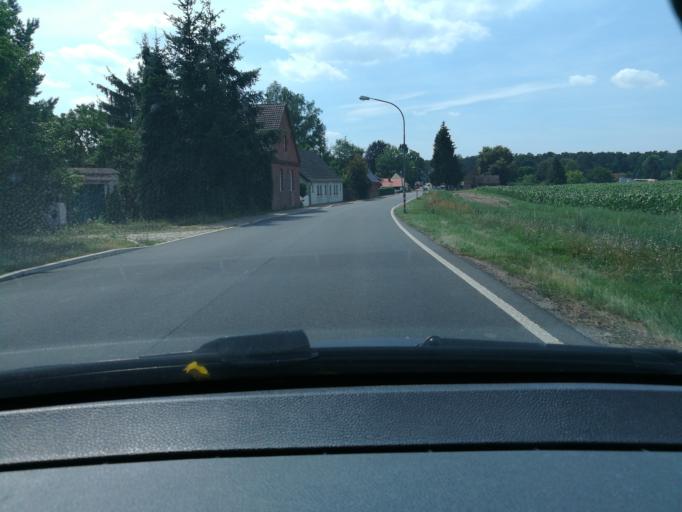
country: DE
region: Brandenburg
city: Kyritz
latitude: 53.0364
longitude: 12.4585
